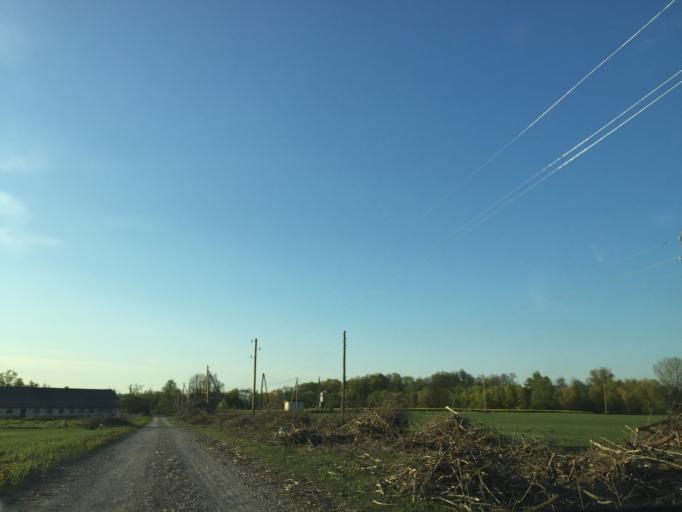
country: LV
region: Bauskas Rajons
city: Bauska
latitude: 56.3140
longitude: 24.1800
